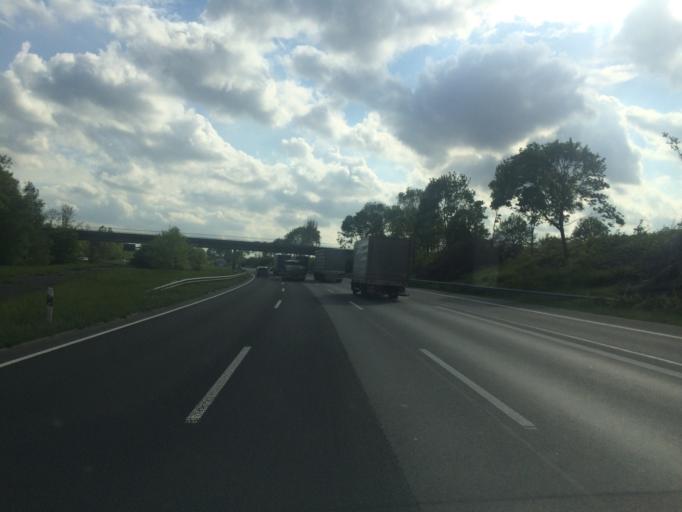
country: DE
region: North Rhine-Westphalia
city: Bad Oeynhausen
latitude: 52.2037
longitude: 8.8354
